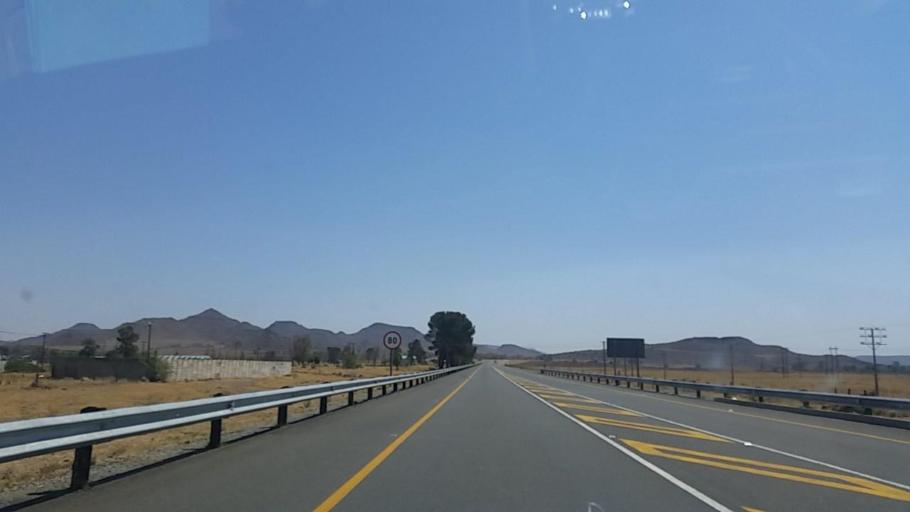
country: ZA
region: Eastern Cape
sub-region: Chris Hani District Municipality
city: Middelburg
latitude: -31.4917
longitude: 25.0155
